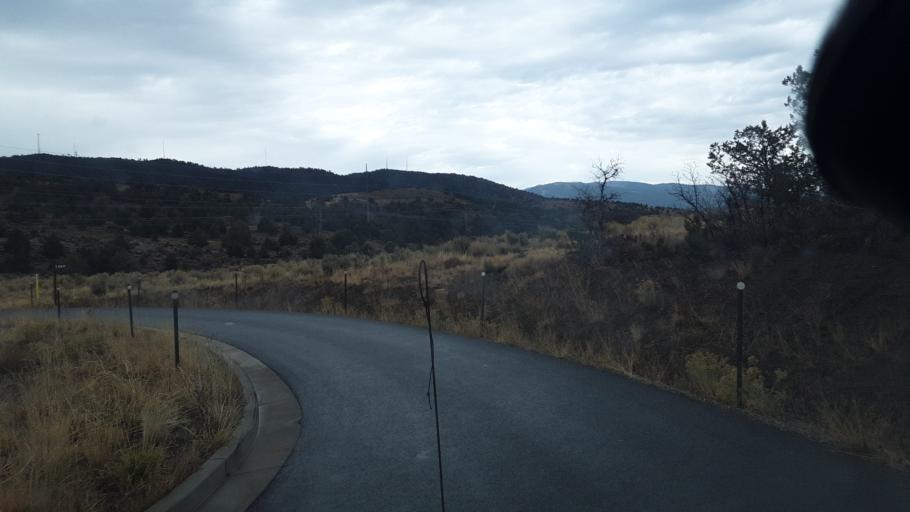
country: US
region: Colorado
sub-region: La Plata County
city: Durango
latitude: 37.2409
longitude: -107.9023
